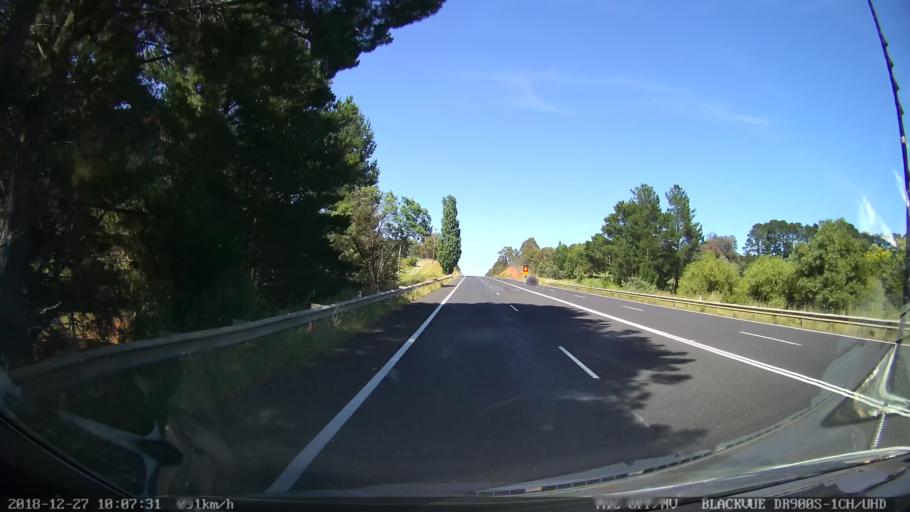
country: AU
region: New South Wales
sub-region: Lithgow
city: Portland
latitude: -33.4405
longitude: 149.8385
